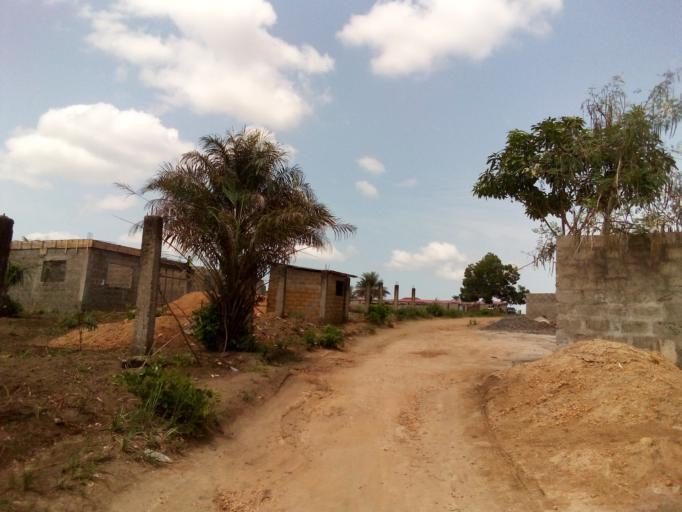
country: SL
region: Western Area
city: Waterloo
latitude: 8.3438
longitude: -13.0260
